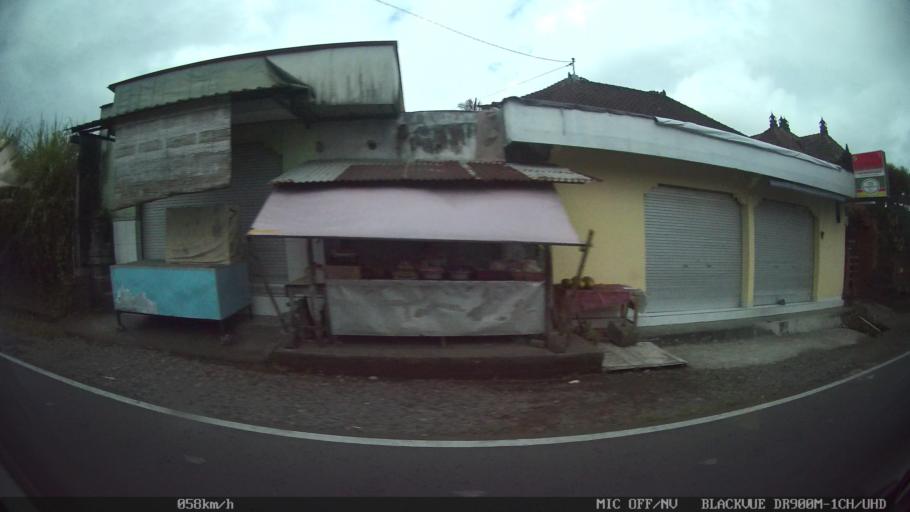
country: ID
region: Bali
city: Banjar Kubu
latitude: -8.3953
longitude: 115.4200
